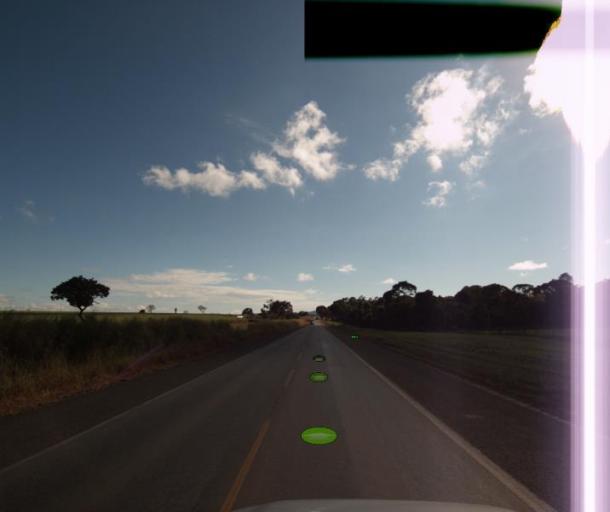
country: BR
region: Goias
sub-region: Uruacu
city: Uruacu
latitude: -14.6506
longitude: -49.1865
